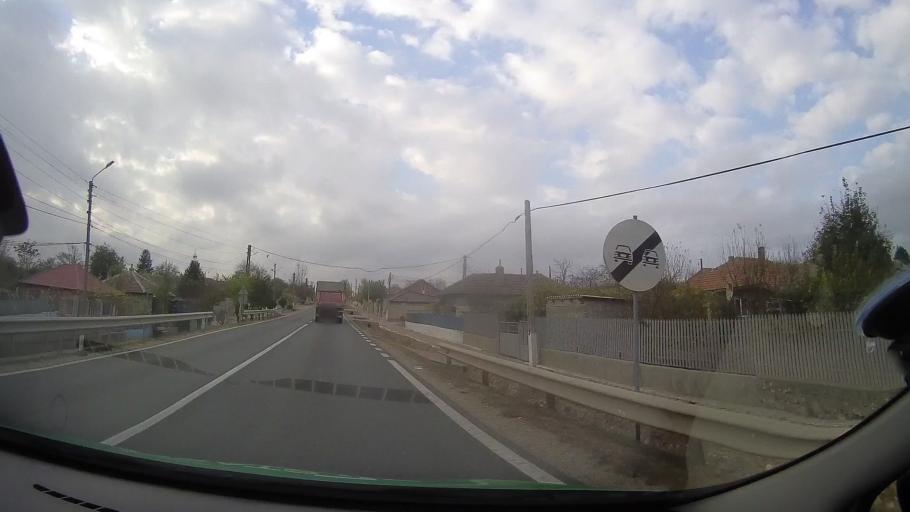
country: RO
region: Constanta
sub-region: Comuna Mircea Voda
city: Satu Nou
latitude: 44.2681
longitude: 28.2239
